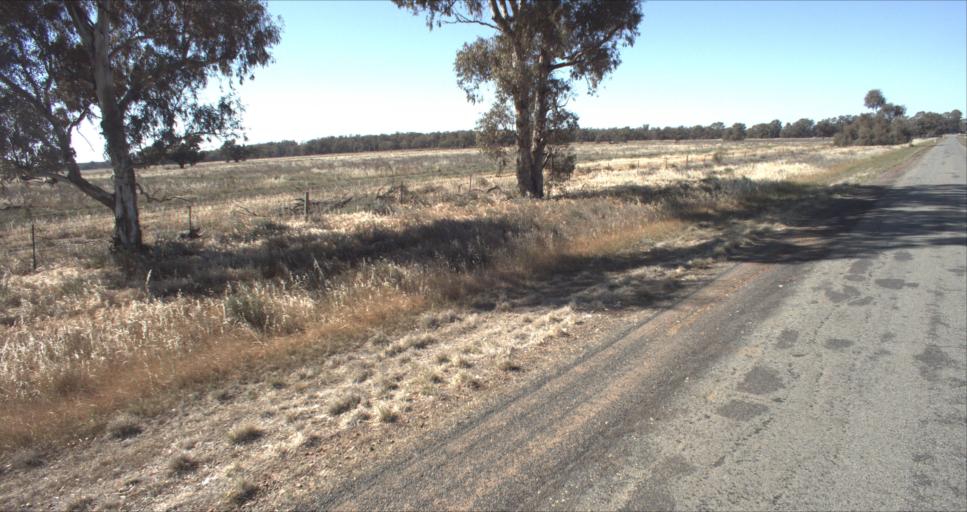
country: AU
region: New South Wales
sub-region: Leeton
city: Leeton
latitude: -34.5985
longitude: 146.2582
